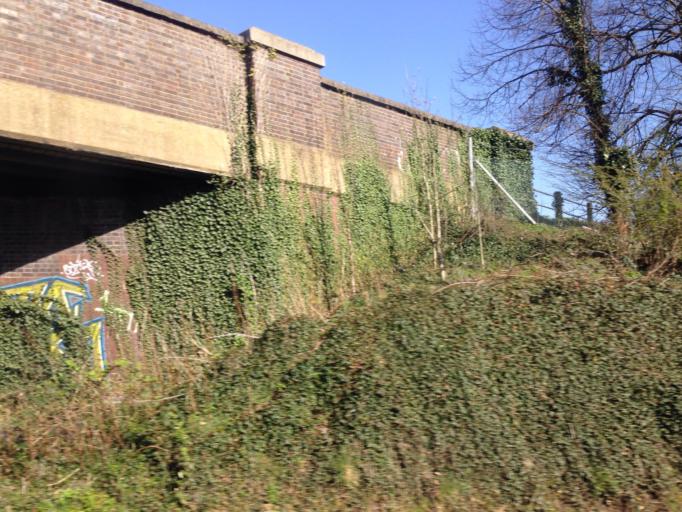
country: GB
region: England
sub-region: Greater London
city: Mitcham
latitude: 51.3989
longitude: -0.1595
